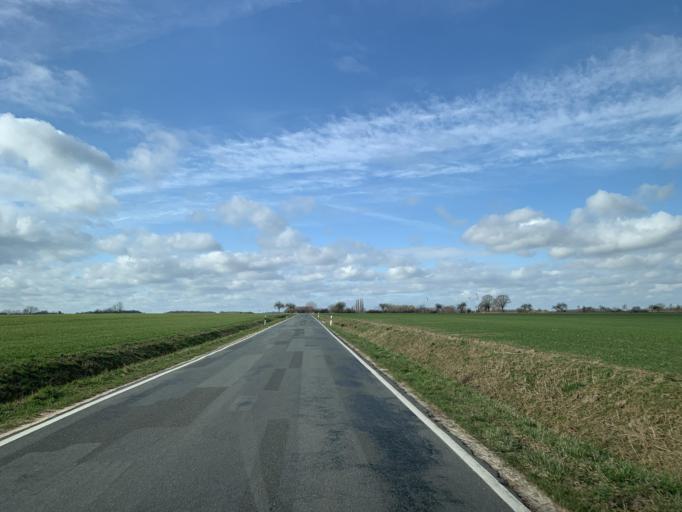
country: DE
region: North Rhine-Westphalia
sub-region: Regierungsbezirk Munster
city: Havixbeck
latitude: 52.0204
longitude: 7.3915
